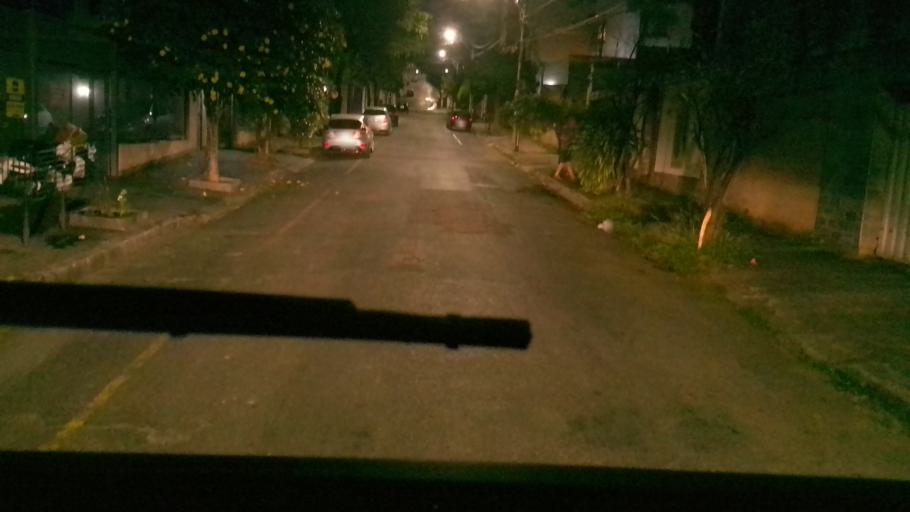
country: BR
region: Minas Gerais
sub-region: Belo Horizonte
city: Belo Horizonte
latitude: -19.8718
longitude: -43.9219
